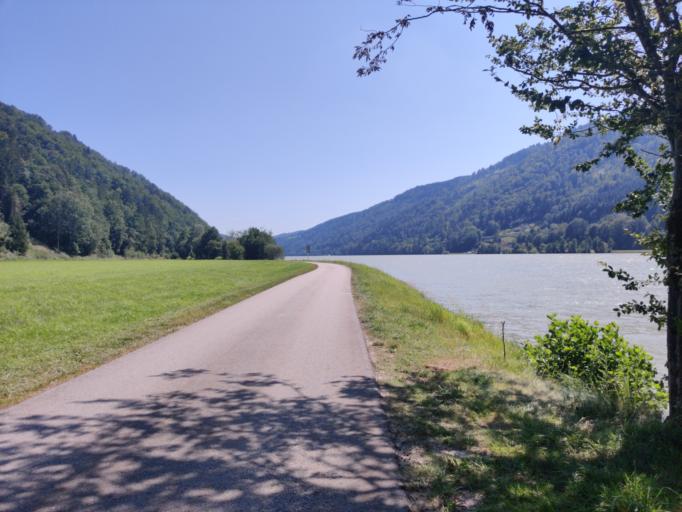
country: AT
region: Upper Austria
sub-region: Politischer Bezirk Rohrbach
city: Pfarrkirchen im Muehlkreis
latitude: 48.4433
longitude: 13.8361
